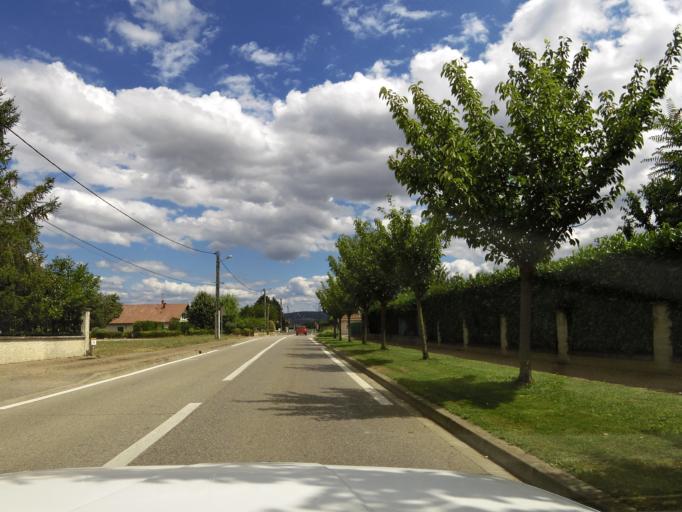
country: FR
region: Rhone-Alpes
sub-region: Departement de l'Ain
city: Loyettes
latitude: 45.7811
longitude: 5.2092
